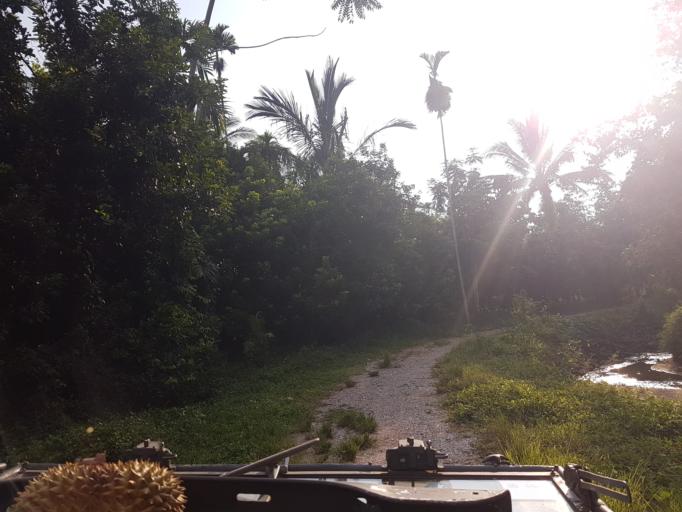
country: TH
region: Pattani
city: Khok Pho
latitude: 6.6653
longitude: 101.0885
